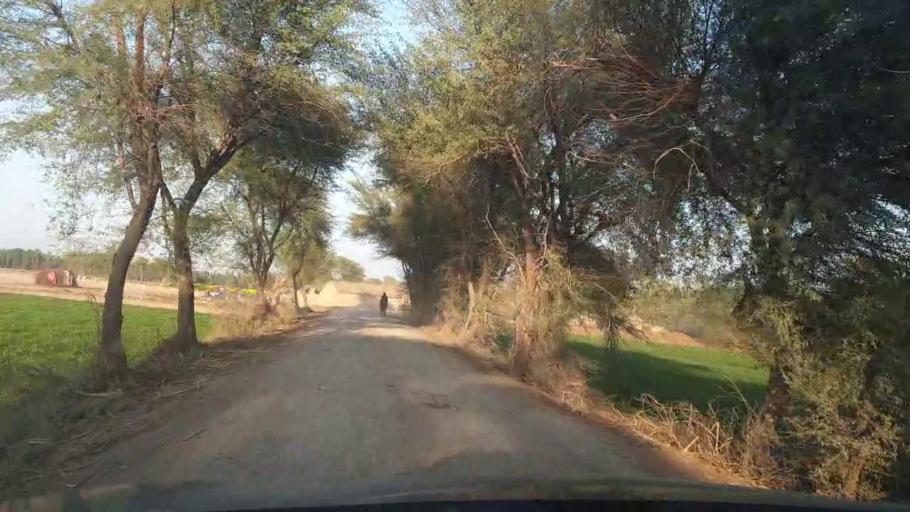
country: PK
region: Sindh
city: Ubauro
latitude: 28.1693
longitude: 69.5797
